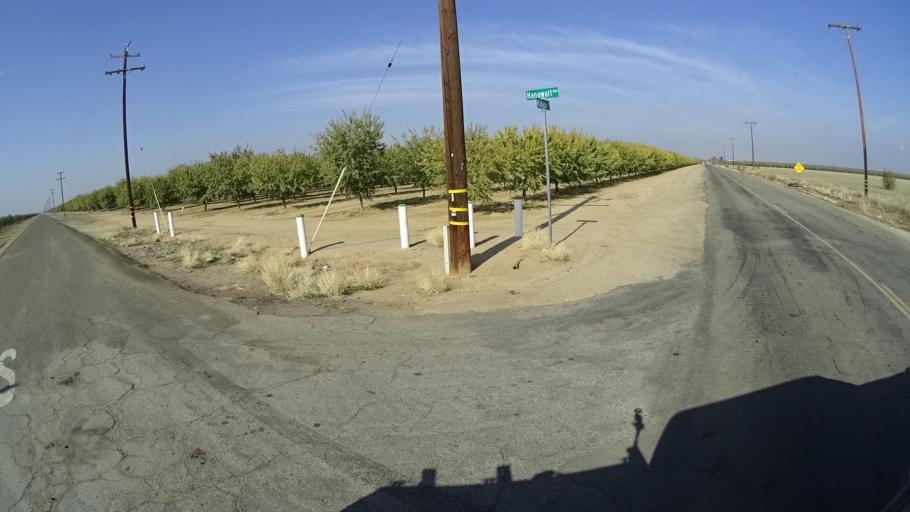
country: US
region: California
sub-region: Kern County
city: McFarland
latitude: 35.6598
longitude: -119.1689
